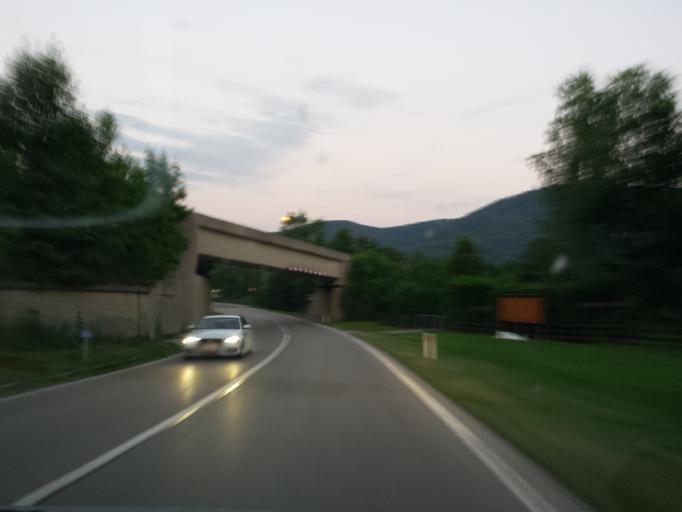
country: AT
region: Lower Austria
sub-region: Politischer Bezirk Baden
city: Altenmarkt an der Triesting
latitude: 48.0205
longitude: 15.9587
